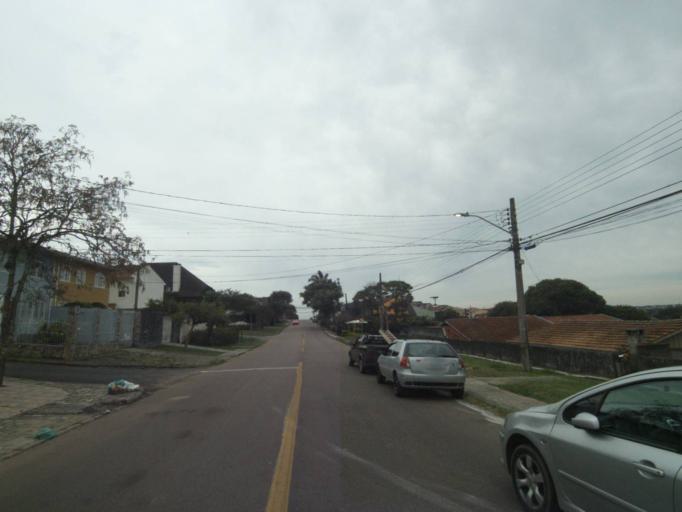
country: BR
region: Parana
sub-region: Pinhais
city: Pinhais
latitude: -25.4217
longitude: -49.2071
